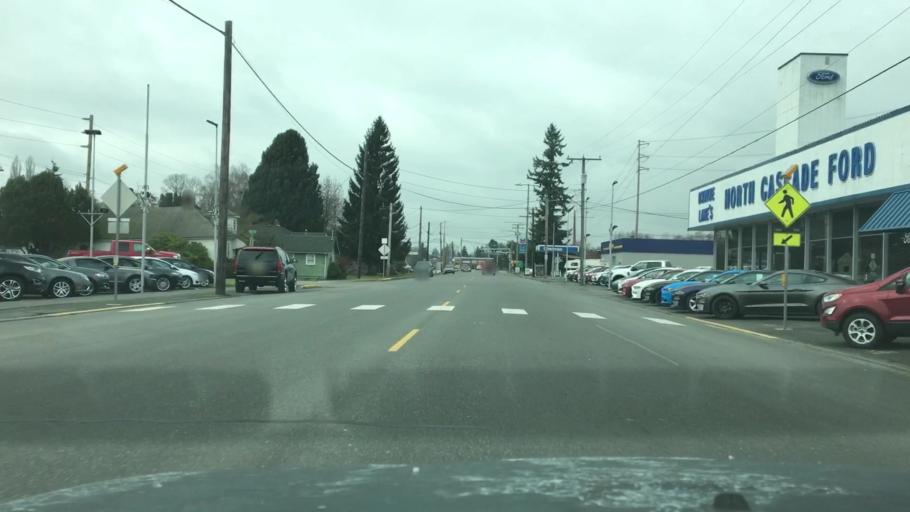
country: US
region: Washington
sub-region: Skagit County
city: Sedro-Woolley
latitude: 48.5054
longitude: -122.2415
